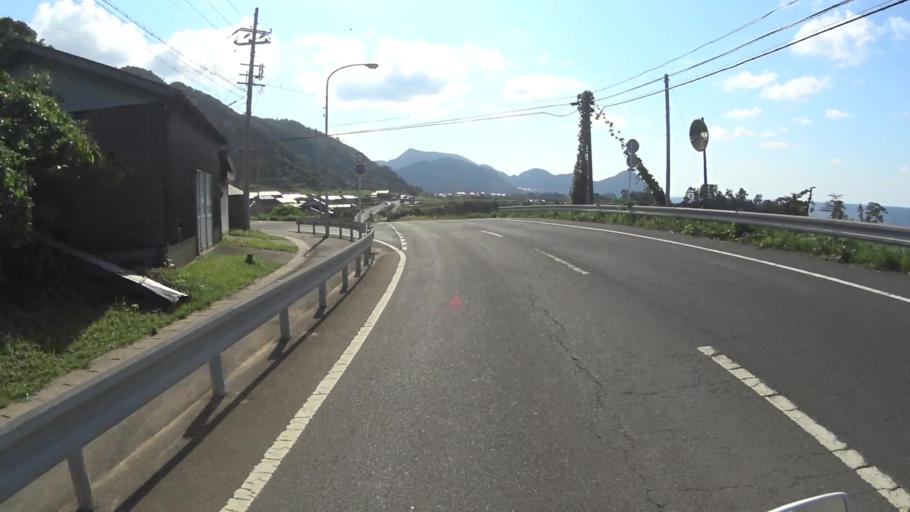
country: JP
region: Kyoto
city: Miyazu
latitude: 35.7646
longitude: 135.1938
